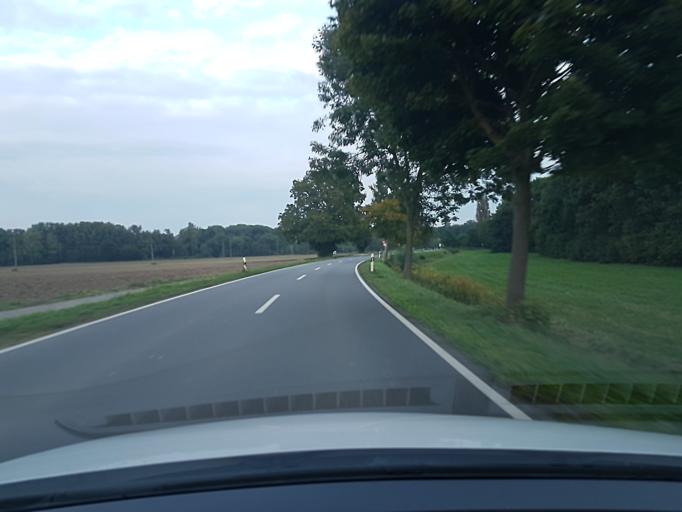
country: DE
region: Rheinland-Pfalz
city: Waldsee
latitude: 49.3978
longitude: 8.4654
